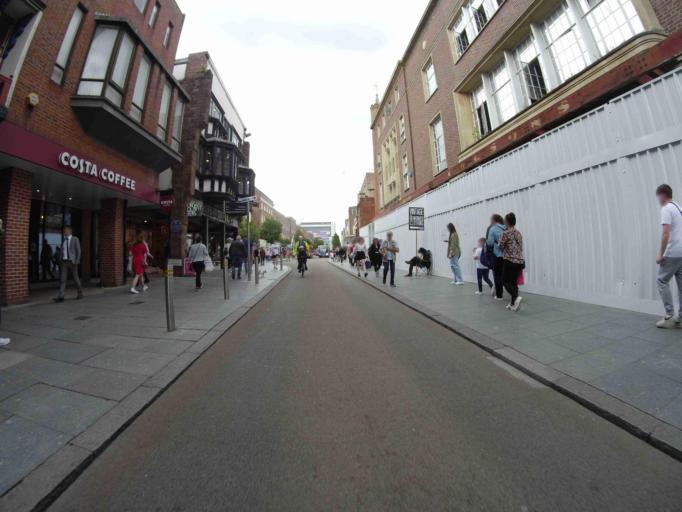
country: GB
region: England
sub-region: Devon
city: Exeter
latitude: 50.7239
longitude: -3.5304
